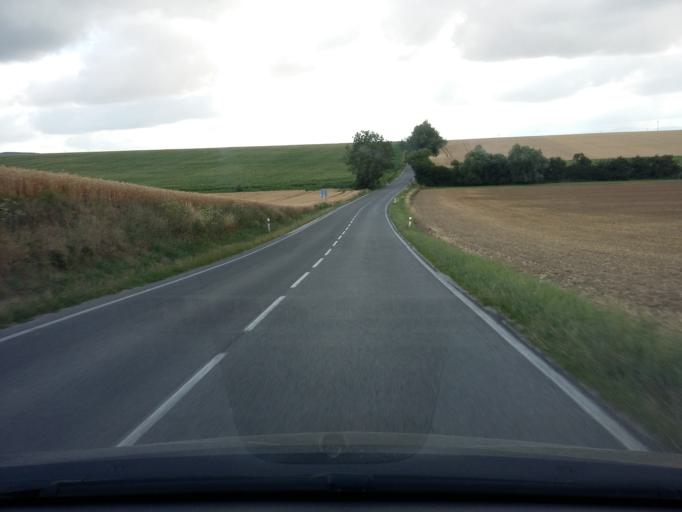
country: SK
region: Trnavsky
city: Vrbove
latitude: 48.5913
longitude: 17.6702
